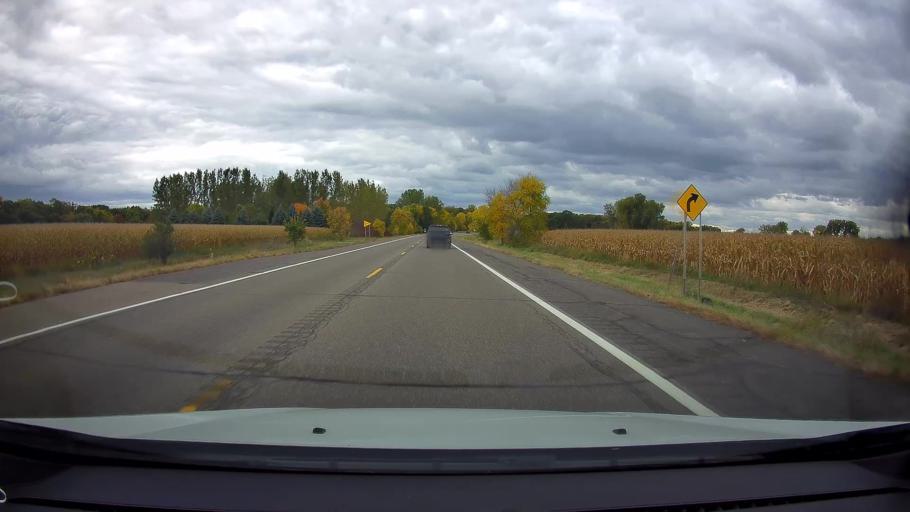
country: US
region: Minnesota
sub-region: Chisago County
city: Chisago City
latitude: 45.3468
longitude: -92.9118
